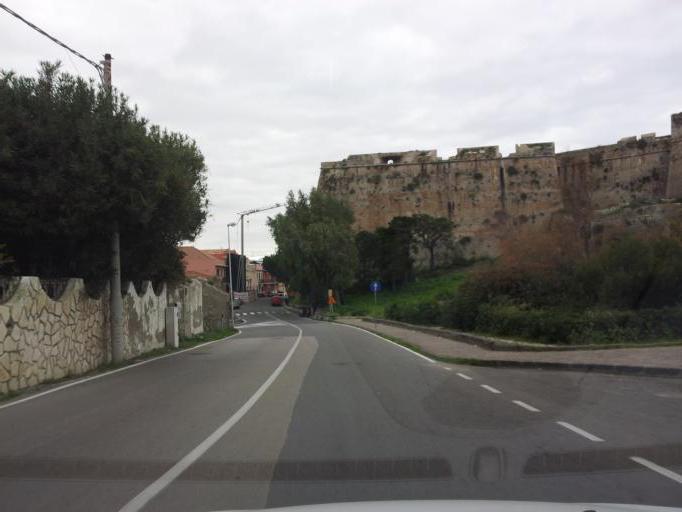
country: IT
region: Sicily
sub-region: Messina
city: Milazzo
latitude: 38.2330
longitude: 15.2446
